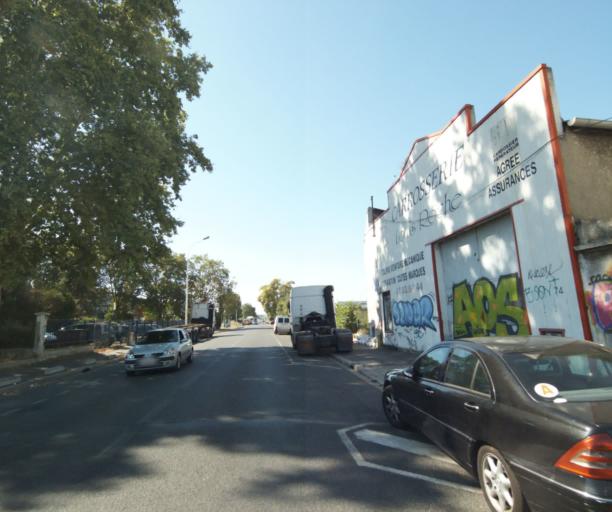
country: FR
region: Ile-de-France
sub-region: Departement des Hauts-de-Seine
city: Villeneuve-la-Garenne
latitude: 48.9248
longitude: 2.3185
